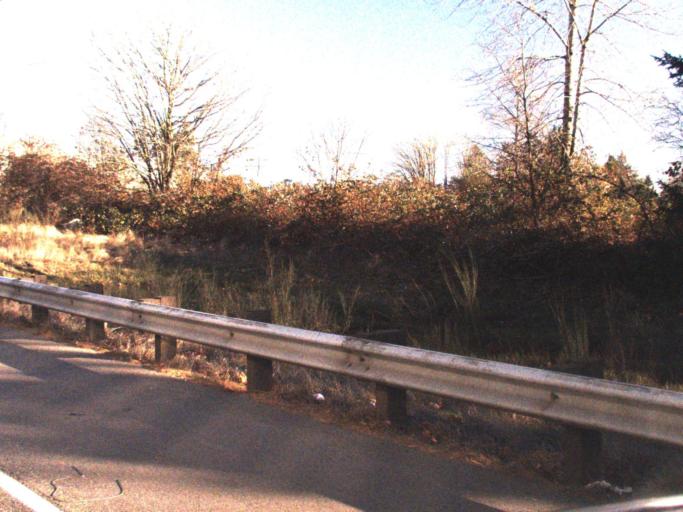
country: US
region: Washington
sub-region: Snohomish County
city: Mill Creek
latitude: 47.8963
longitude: -122.2150
